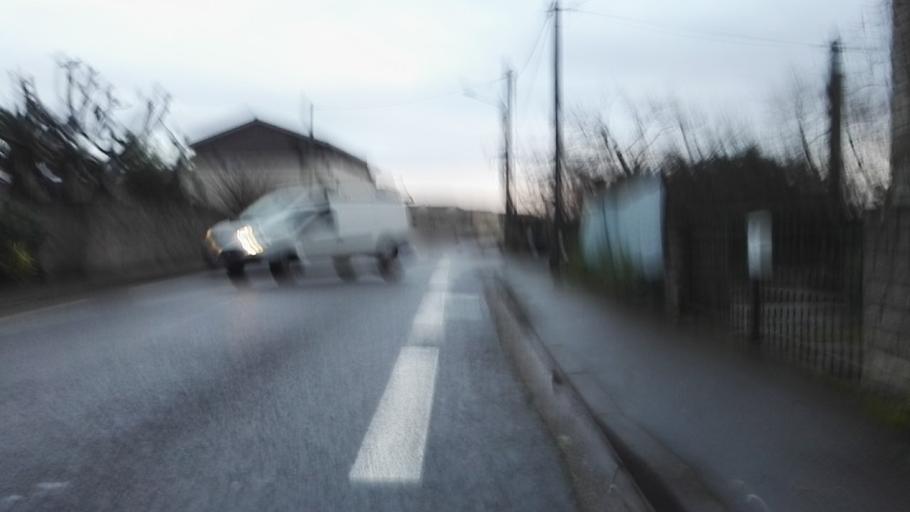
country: FR
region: Aquitaine
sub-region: Departement de la Gironde
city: Merignac
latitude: 44.8316
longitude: -0.6342
